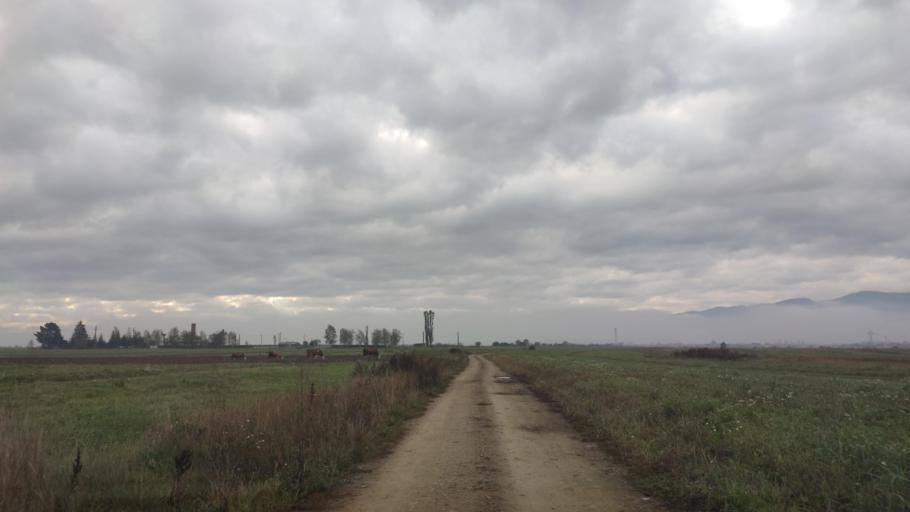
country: RO
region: Harghita
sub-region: Comuna Ciumani
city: Ciumani
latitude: 46.6992
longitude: 25.5189
